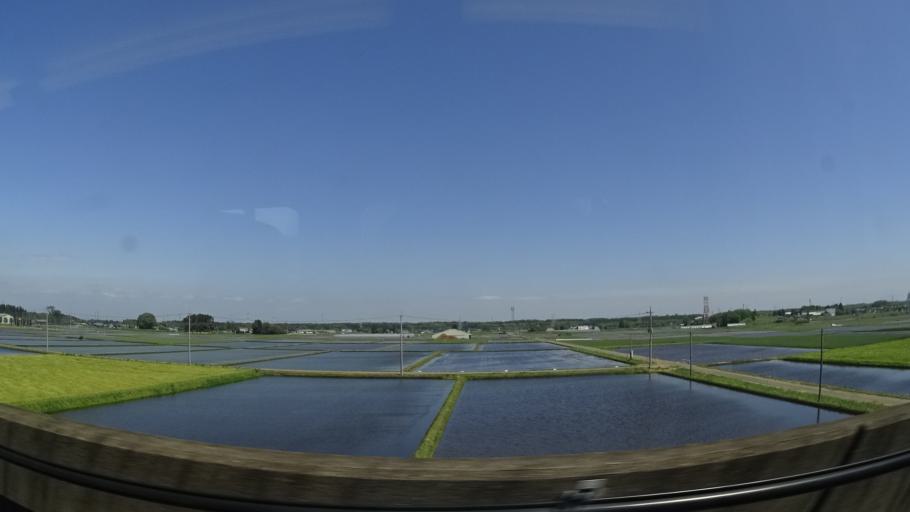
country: JP
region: Tochigi
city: Ujiie
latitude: 36.6412
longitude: 139.9109
